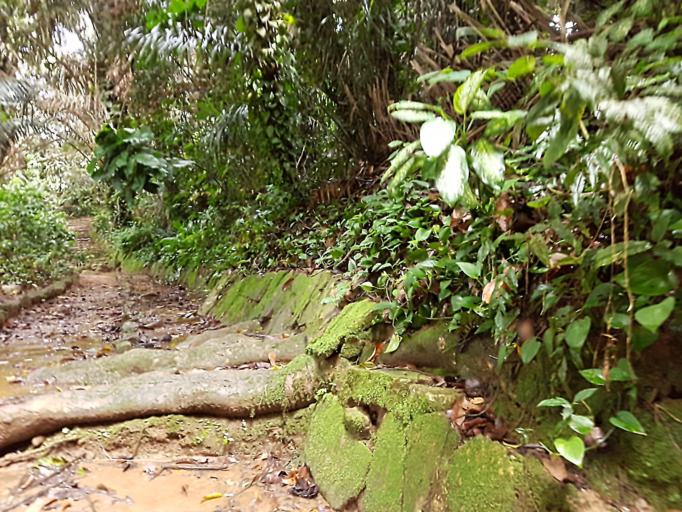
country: UG
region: Central Region
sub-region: Wakiso District
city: Entebbe
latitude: 0.0624
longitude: 32.4786
